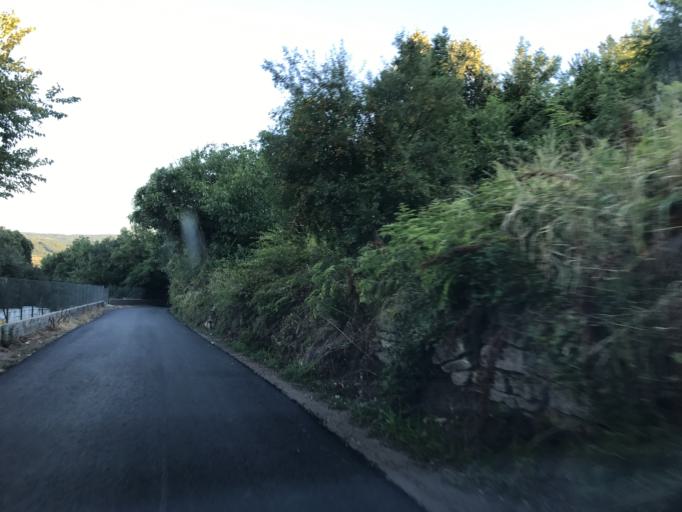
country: BG
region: Vidin
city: Bregovo
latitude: 44.1229
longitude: 22.5990
